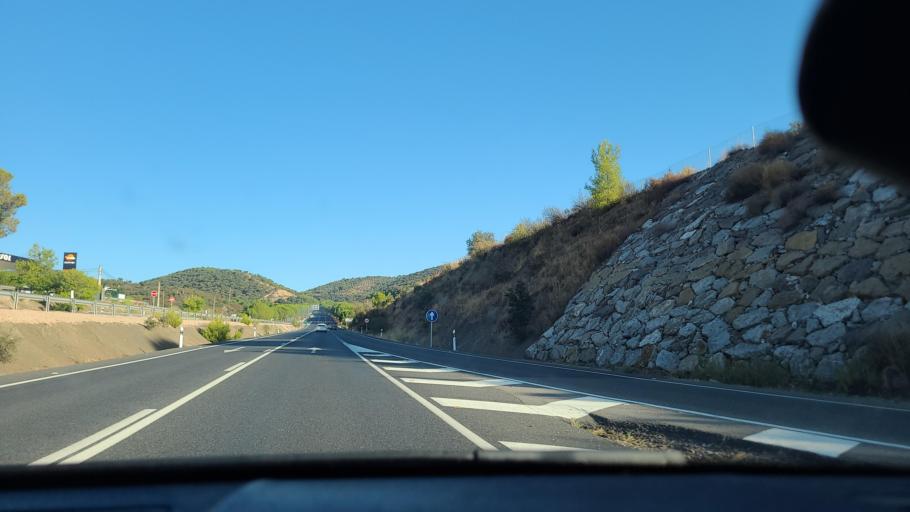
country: ES
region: Andalusia
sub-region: Province of Cordoba
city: Villaharta
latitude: 38.1252
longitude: -4.9008
